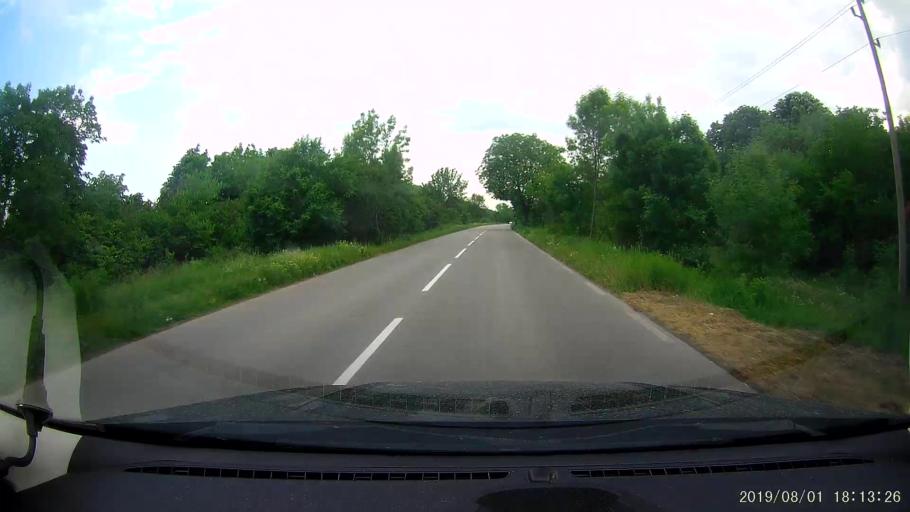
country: BG
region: Silistra
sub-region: Obshtina Dulovo
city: Dulovo
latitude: 43.7893
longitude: 27.1396
